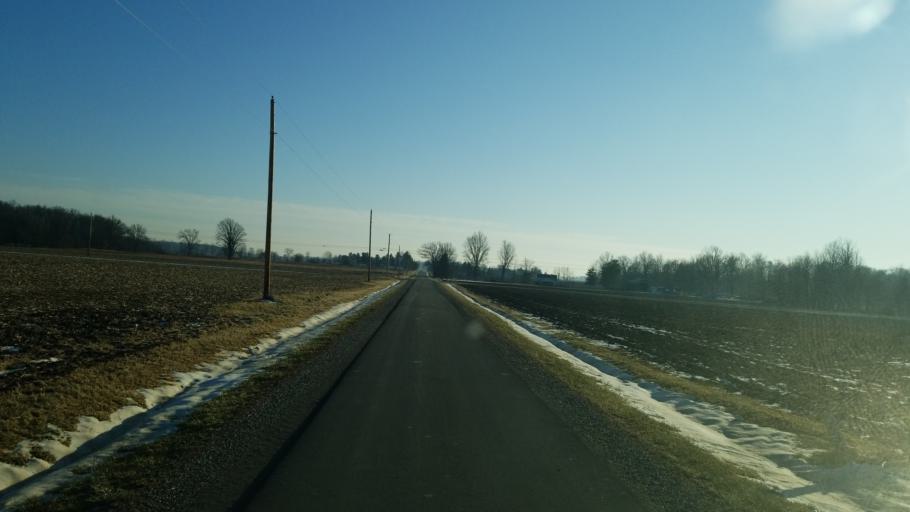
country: US
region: Ohio
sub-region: Crawford County
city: Bucyrus
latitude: 40.9526
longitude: -82.9208
